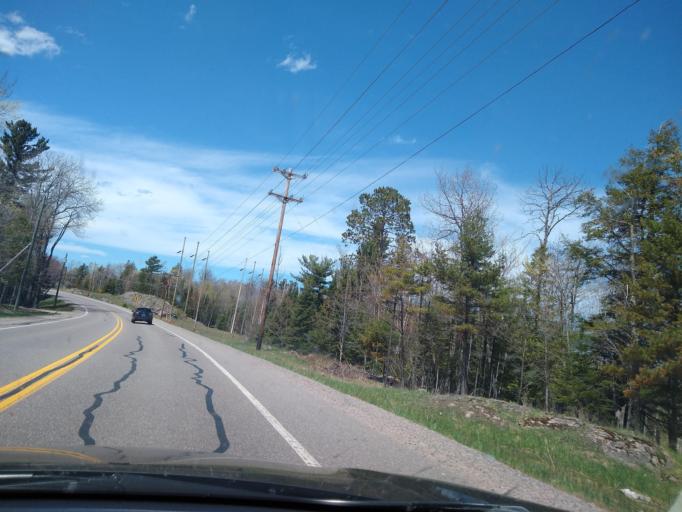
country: US
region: Michigan
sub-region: Marquette County
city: Trowbridge Park
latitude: 46.5773
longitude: -87.4233
